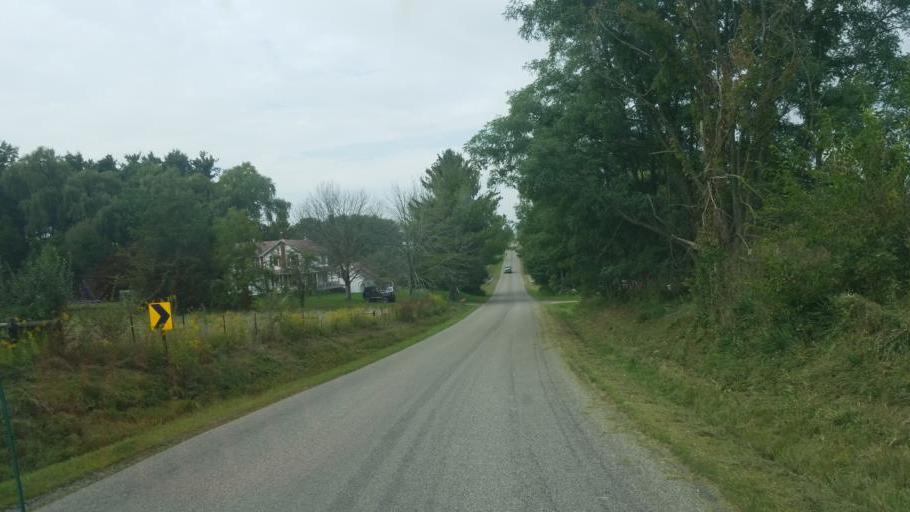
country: US
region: Ohio
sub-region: Wayne County
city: West Salem
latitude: 40.9313
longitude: -82.0551
